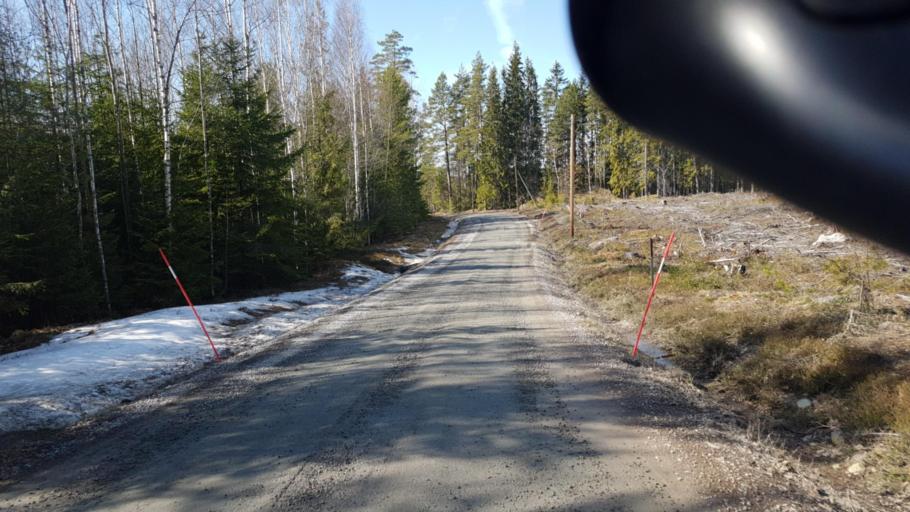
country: SE
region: Vaermland
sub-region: Arvika Kommun
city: Arvika
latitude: 59.6024
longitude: 12.7770
